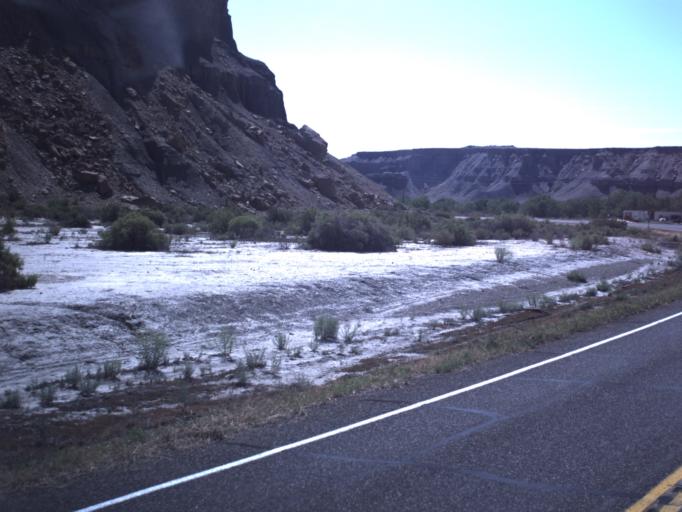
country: US
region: Utah
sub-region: Wayne County
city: Loa
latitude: 38.3608
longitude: -110.8766
